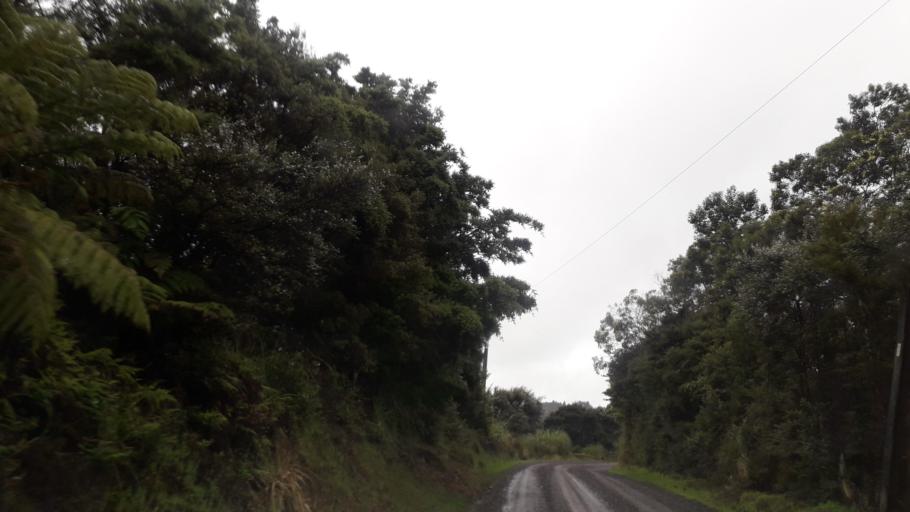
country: NZ
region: Northland
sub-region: Far North District
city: Kaitaia
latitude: -35.3809
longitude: 173.4097
